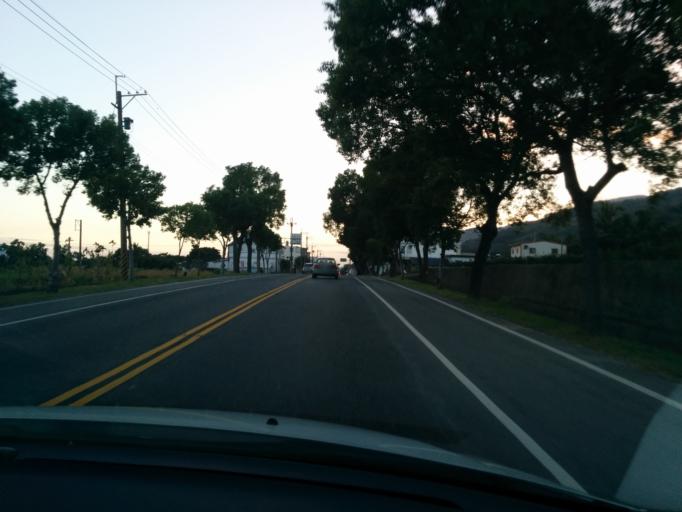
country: TW
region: Taiwan
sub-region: Taitung
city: Taitung
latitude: 22.9912
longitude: 121.1423
